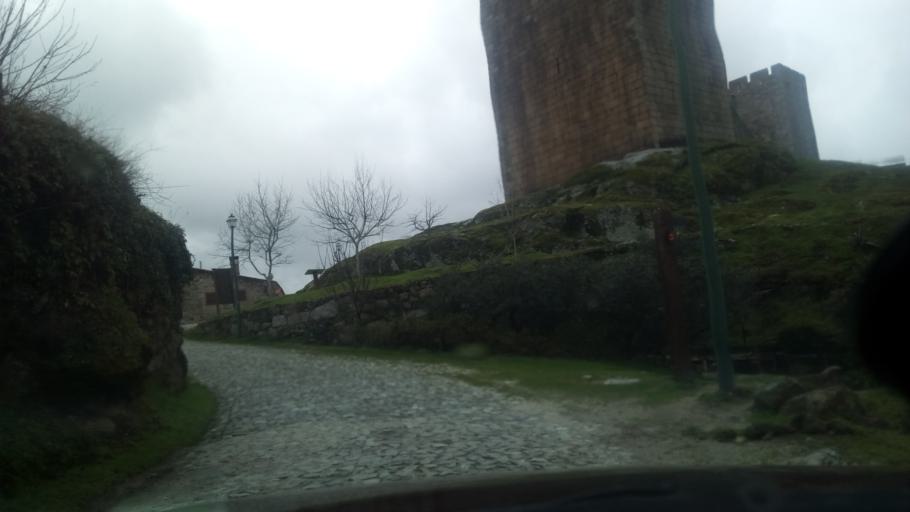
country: PT
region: Guarda
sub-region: Fornos de Algodres
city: Fornos de Algodres
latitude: 40.5414
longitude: -7.4605
